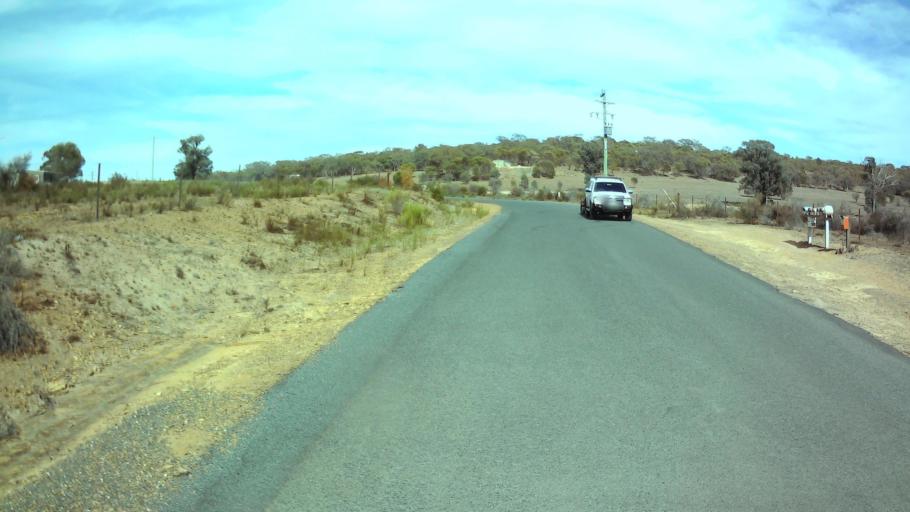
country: AU
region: New South Wales
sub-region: Weddin
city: Grenfell
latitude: -33.8774
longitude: 148.2010
